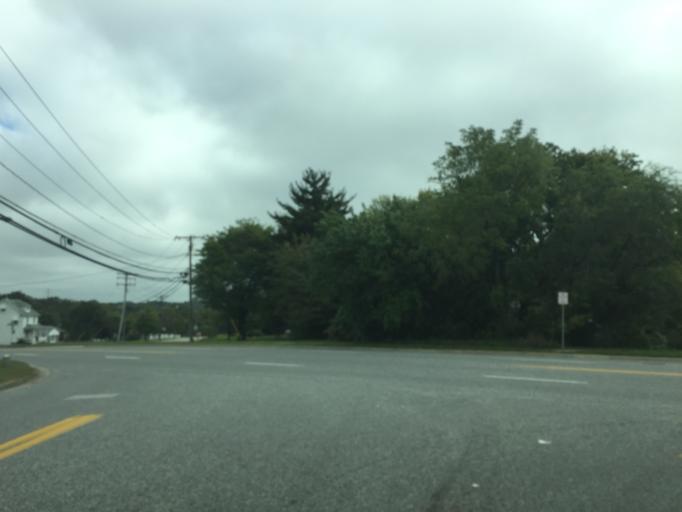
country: US
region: Maryland
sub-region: Baltimore County
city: Rossville
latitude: 39.3306
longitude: -76.4814
